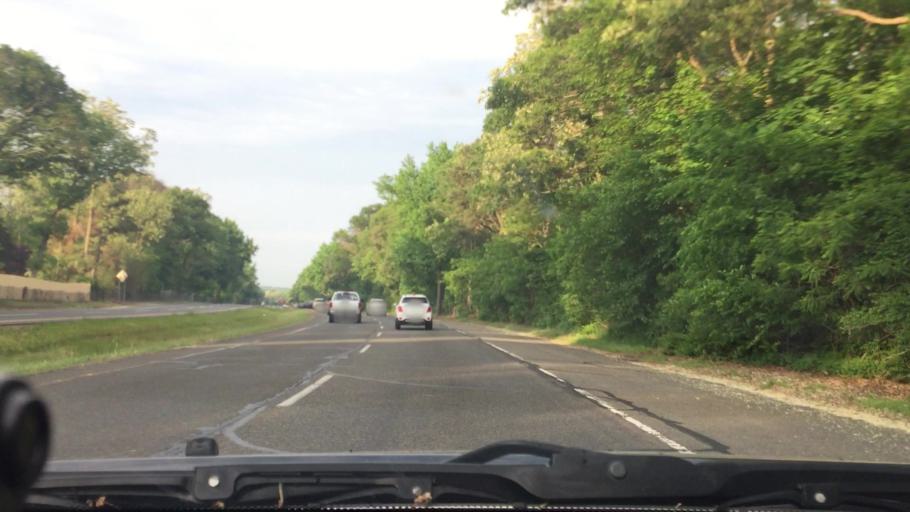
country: US
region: New York
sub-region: Suffolk County
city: Coram
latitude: 40.8811
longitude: -73.0183
